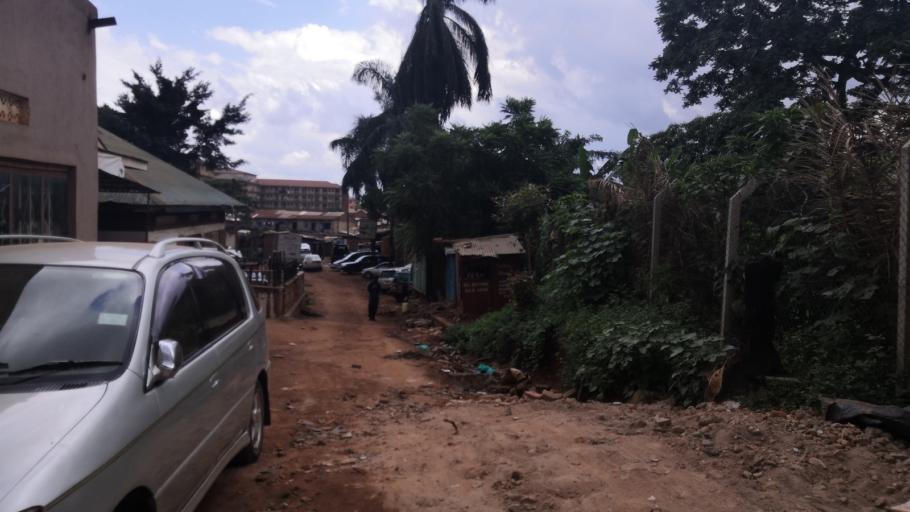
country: UG
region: Central Region
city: Kampala Central Division
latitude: 0.3331
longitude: 32.5754
